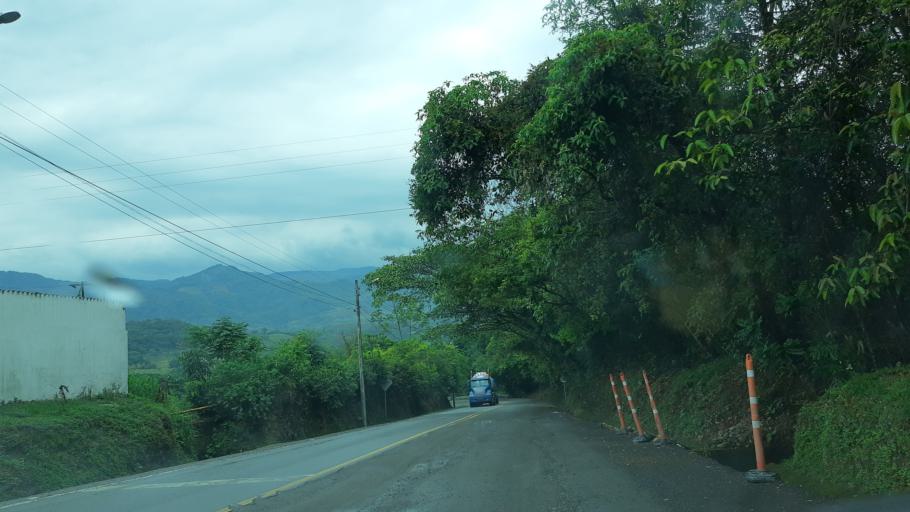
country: CO
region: Casanare
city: Monterrey
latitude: 4.8857
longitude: -72.8949
